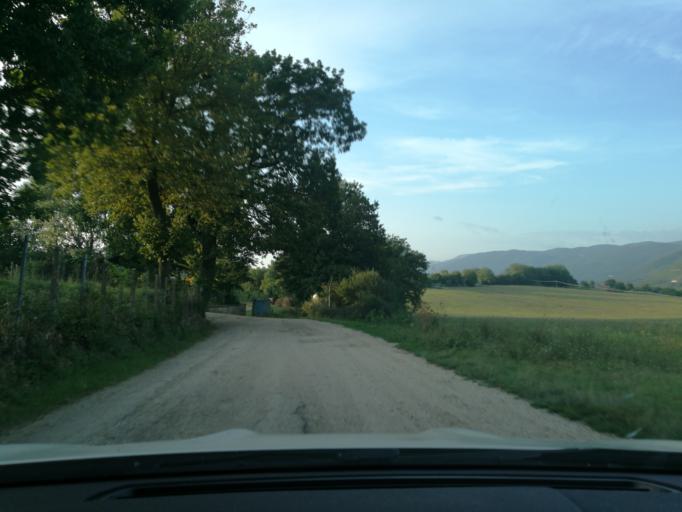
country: IT
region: Umbria
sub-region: Provincia di Terni
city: Acquasparta
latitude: 42.6785
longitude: 12.5453
